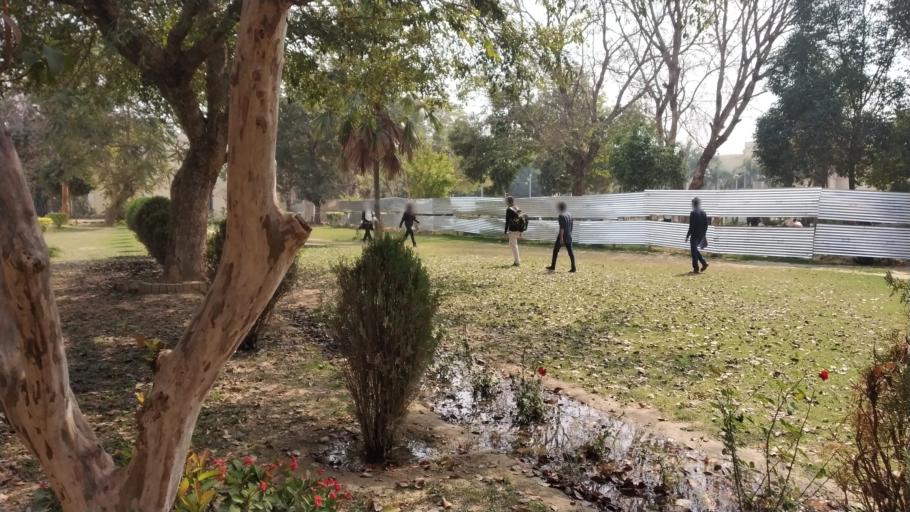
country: IN
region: Uttar Pradesh
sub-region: Allahabad
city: Allahabad
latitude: 25.4929
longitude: 81.8649
